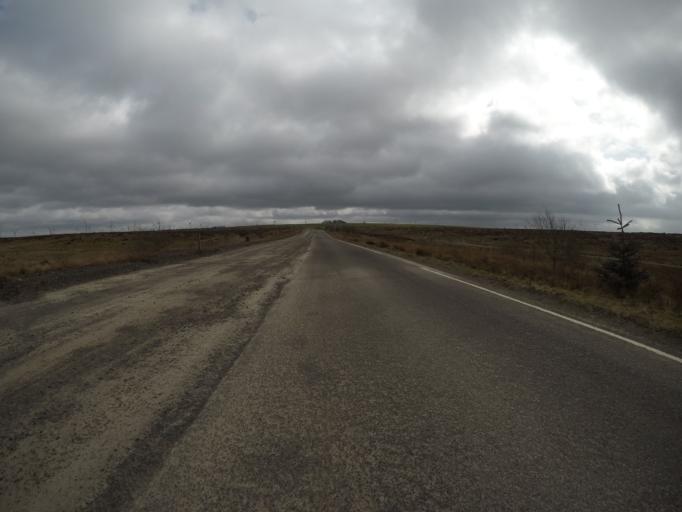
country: GB
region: Scotland
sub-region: East Renfrewshire
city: Newton Mearns
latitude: 55.6991
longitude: -4.3493
